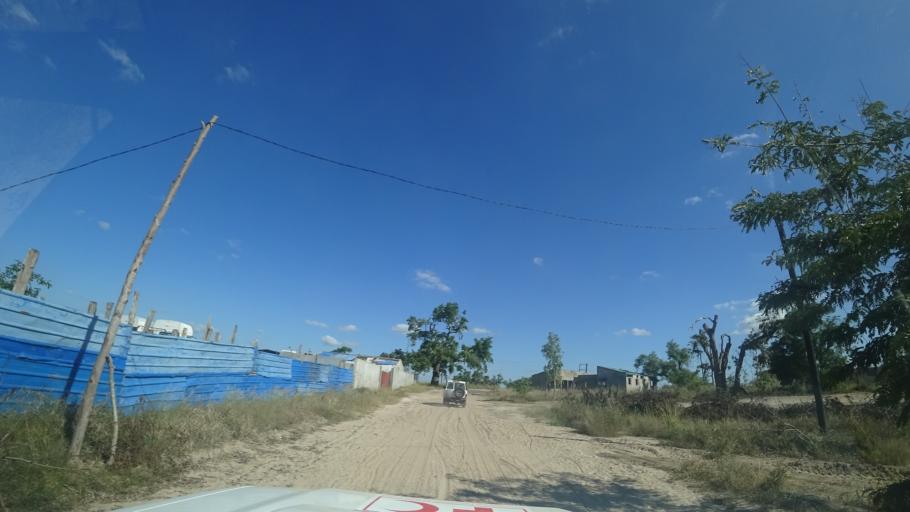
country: MZ
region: Sofala
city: Dondo
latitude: -19.5077
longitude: 34.6097
